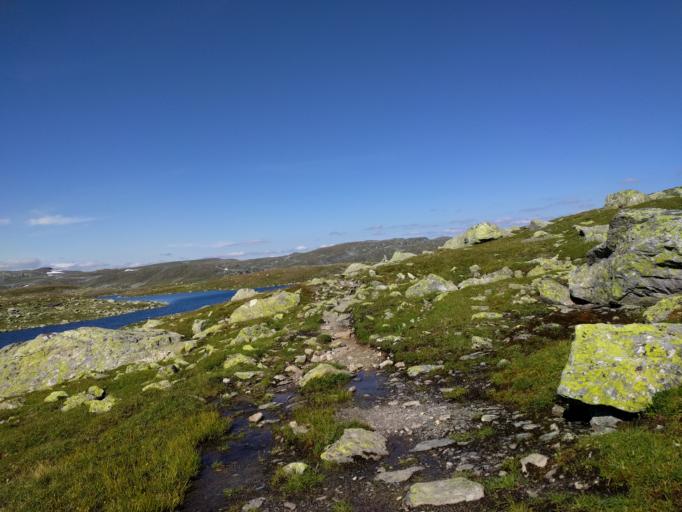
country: NO
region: Aust-Agder
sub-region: Bykle
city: Hovden
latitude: 59.8880
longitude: 7.2072
